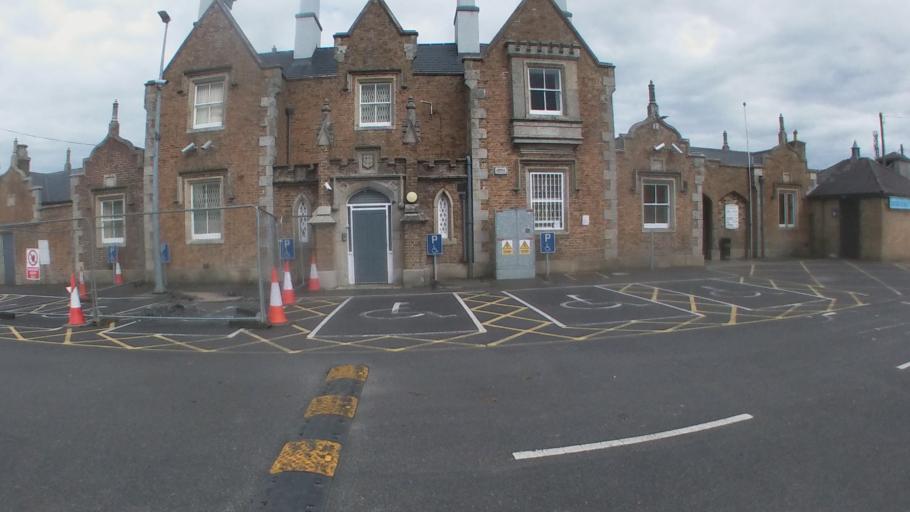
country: IE
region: Leinster
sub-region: County Carlow
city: Carlow
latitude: 52.8408
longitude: -6.9229
